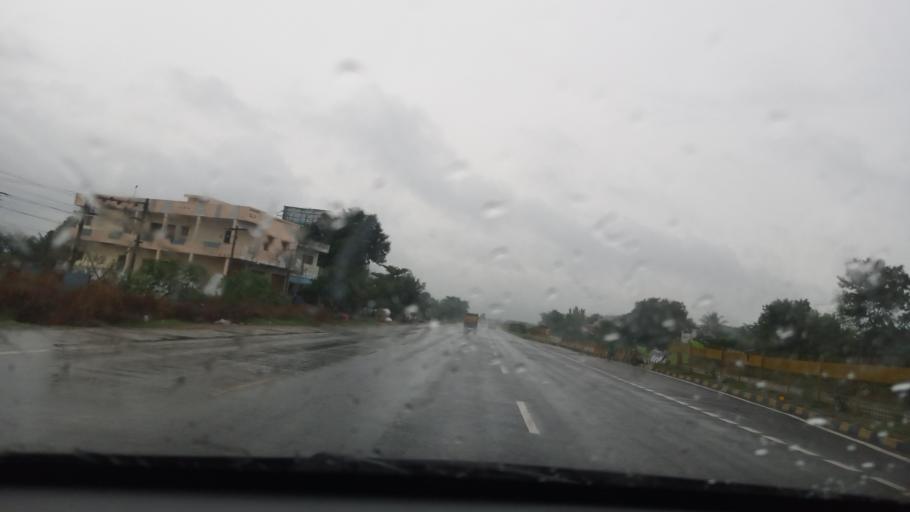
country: IN
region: Tamil Nadu
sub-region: Vellore
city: Pallikondai
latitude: 12.9150
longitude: 79.0233
